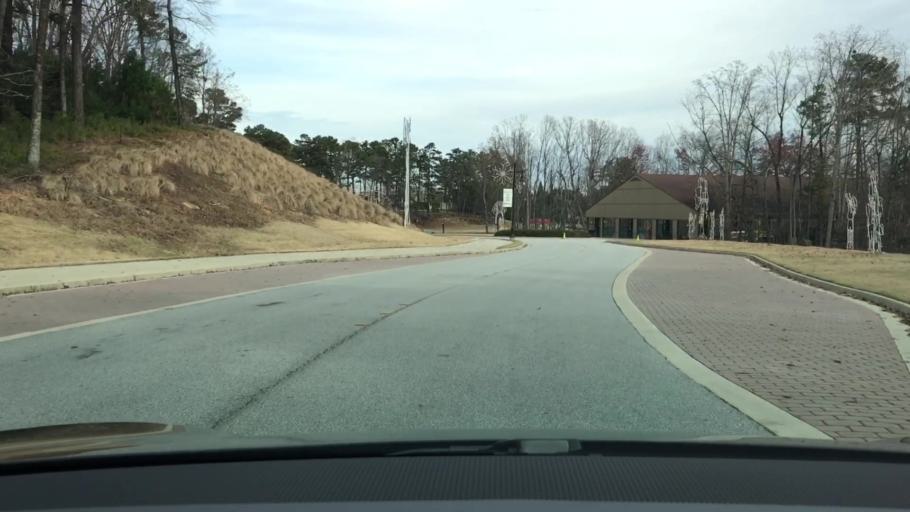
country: US
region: Georgia
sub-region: Gwinnett County
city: Buford
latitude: 34.1804
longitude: -84.0320
